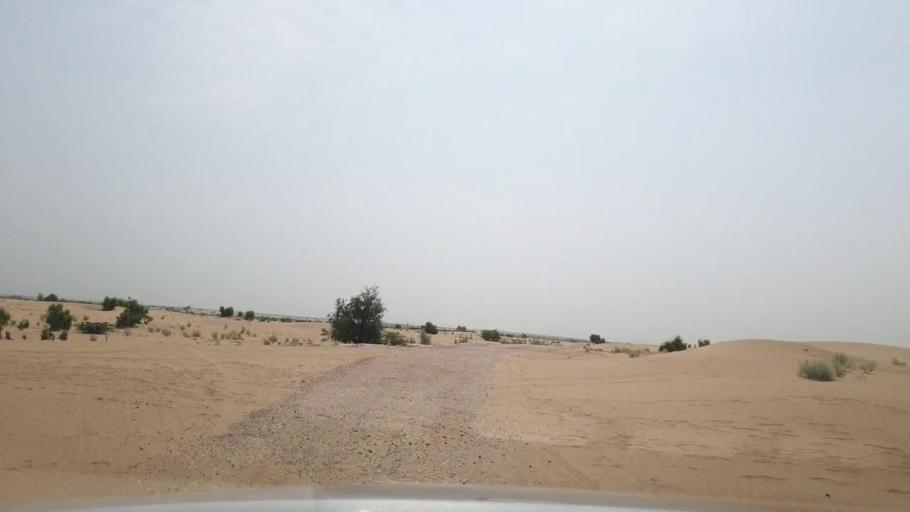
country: PK
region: Sindh
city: Pano Aqil
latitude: 27.6100
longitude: 69.1491
